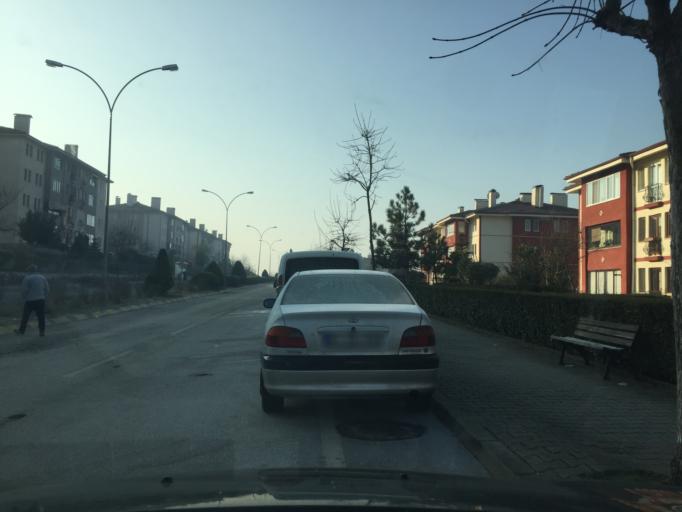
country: TR
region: Duzce
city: Duzce
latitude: 40.8647
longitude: 31.2300
